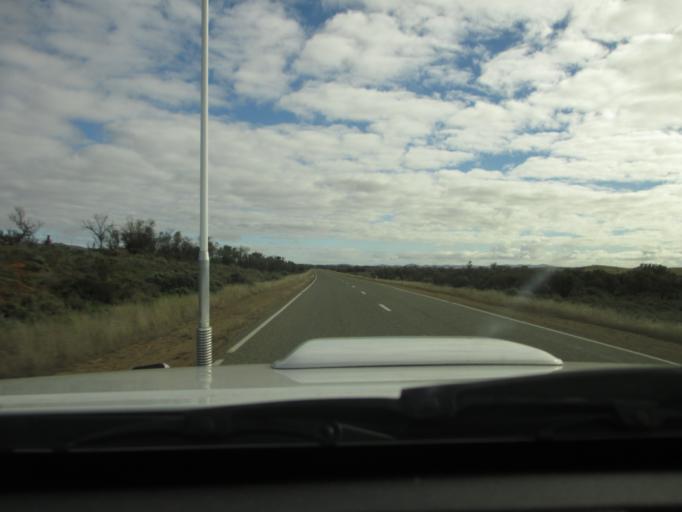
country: AU
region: South Australia
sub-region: Flinders Ranges
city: Quorn
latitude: -32.3937
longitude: 138.5092
